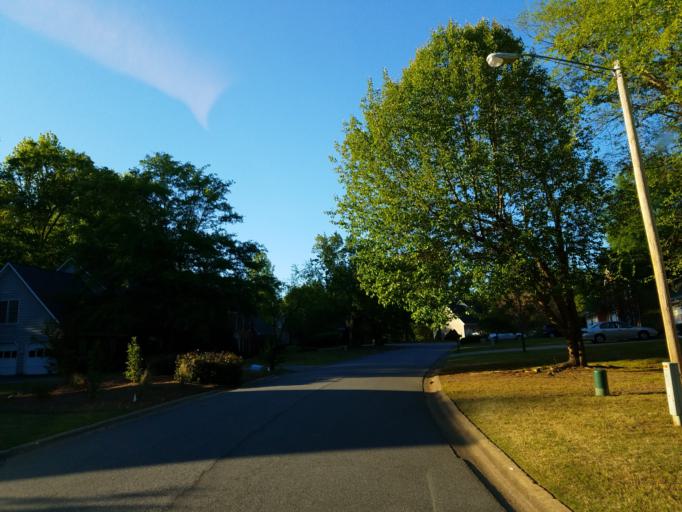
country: US
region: Georgia
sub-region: Cobb County
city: Powder Springs
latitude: 33.9201
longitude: -84.6432
